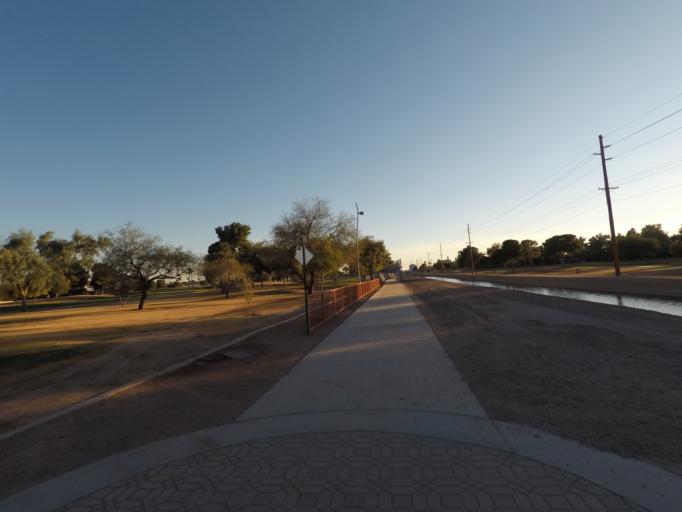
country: US
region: Arizona
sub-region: Maricopa County
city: Guadalupe
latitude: 33.3610
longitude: -111.9380
